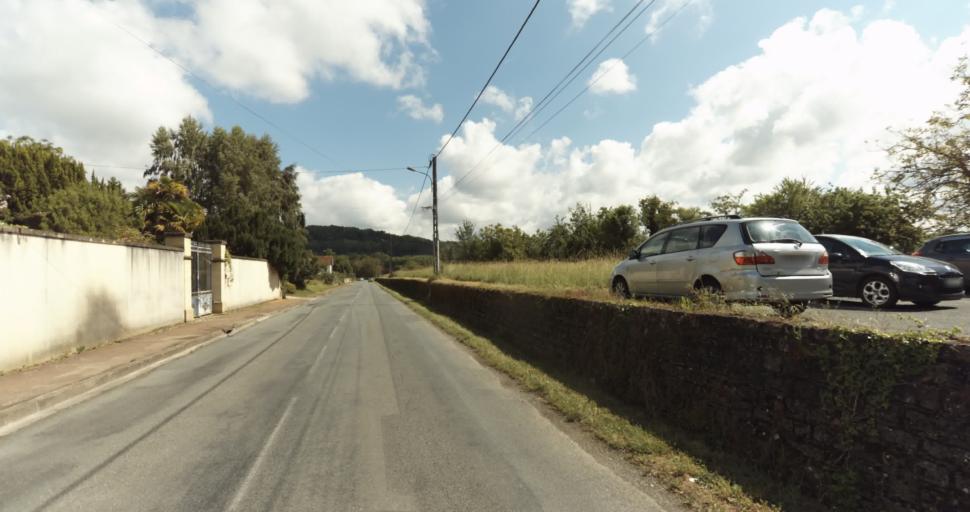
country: FR
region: Aquitaine
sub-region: Departement de la Dordogne
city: Le Bugue
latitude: 44.8490
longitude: 0.9092
